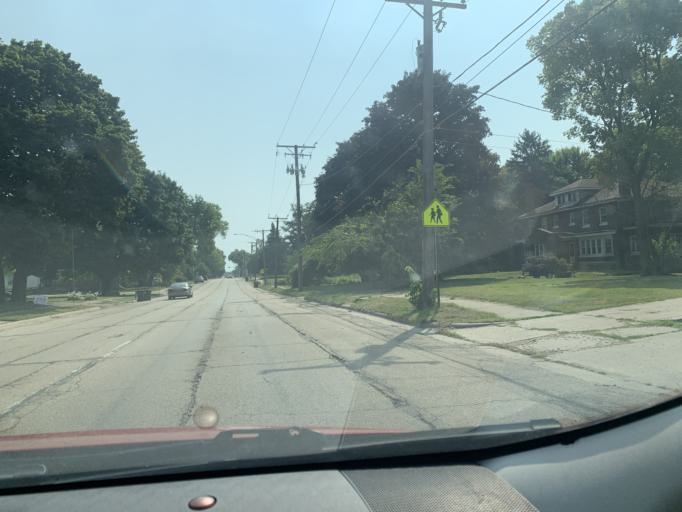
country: US
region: Illinois
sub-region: Whiteside County
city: Sterling
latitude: 41.7889
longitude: -89.7098
